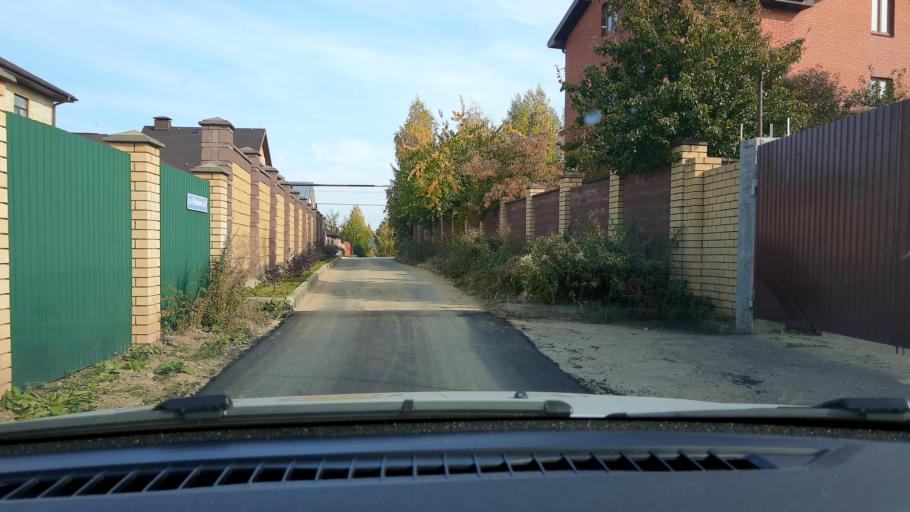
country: RU
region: Nizjnij Novgorod
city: Afonino
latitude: 56.2581
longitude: 44.0879
